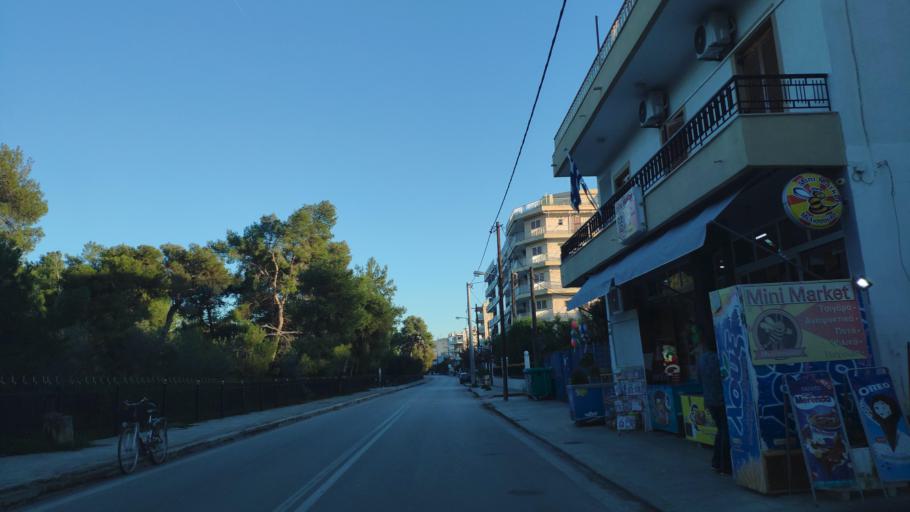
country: GR
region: Peloponnese
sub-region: Nomos Korinthias
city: Xylokastro
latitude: 38.0744
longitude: 22.6409
